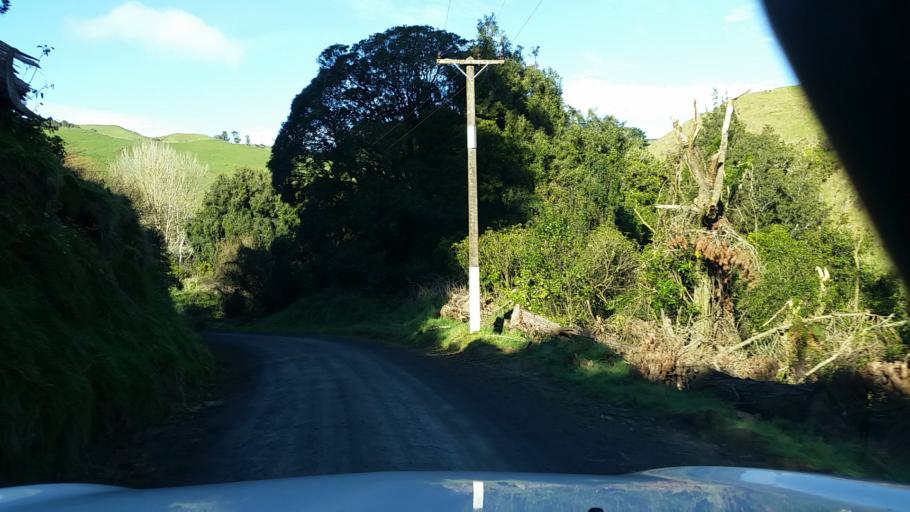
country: NZ
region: Taranaki
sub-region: South Taranaki District
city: Eltham
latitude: -39.5085
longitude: 174.3971
